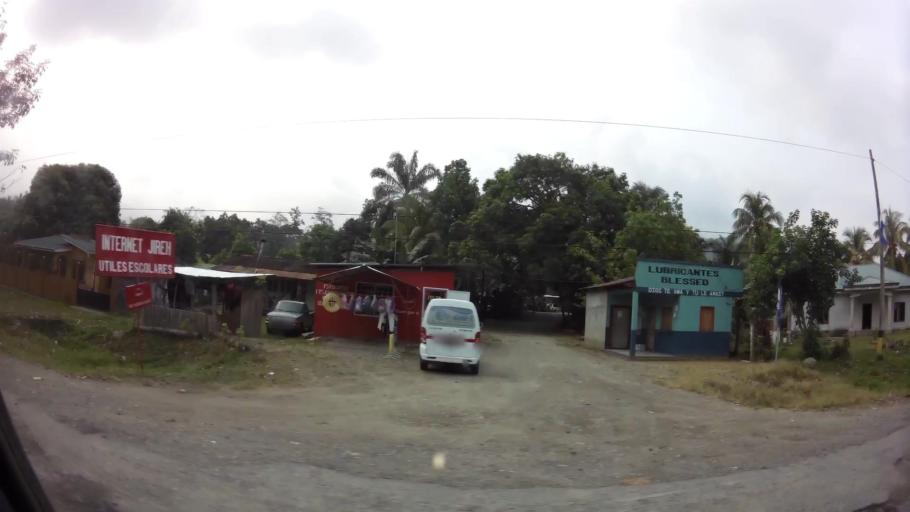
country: HN
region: Yoro
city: Toyos
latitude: 15.5260
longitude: -87.6556
